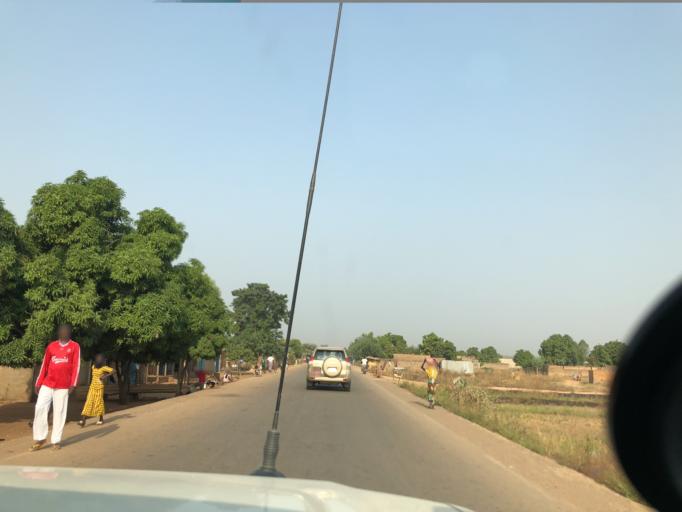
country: TD
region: Logone Occidental
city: Moundou
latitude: 8.5705
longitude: 16.0465
